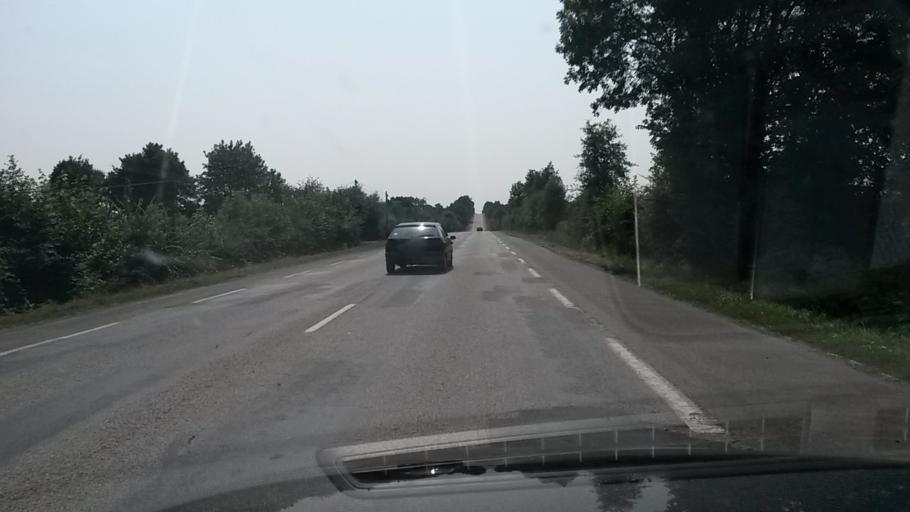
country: FR
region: Pays de la Loire
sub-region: Departement de la Mayenne
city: Chateau-Gontier
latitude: 47.8827
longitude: -0.6833
